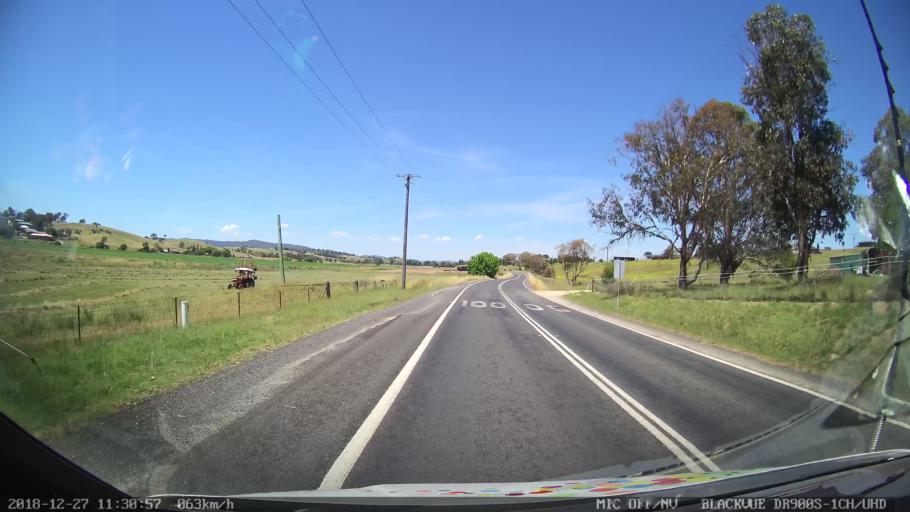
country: AU
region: New South Wales
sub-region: Bathurst Regional
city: Perthville
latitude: -33.4904
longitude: 149.5419
